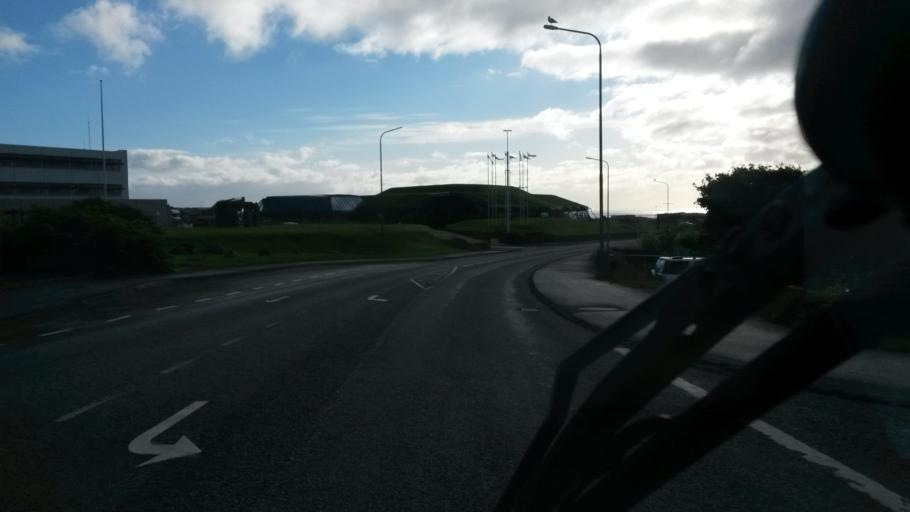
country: FO
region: Streymoy
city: Hoyvik
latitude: 62.0215
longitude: -6.7874
